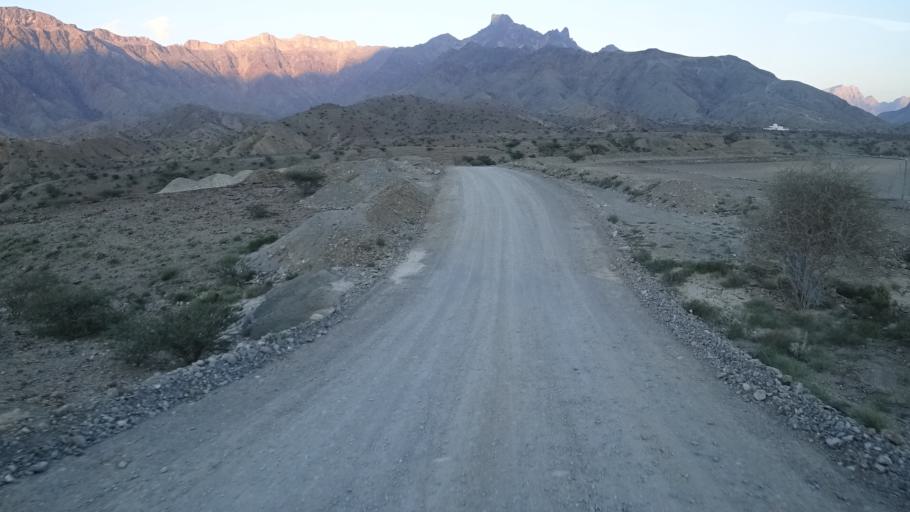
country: OM
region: Al Batinah
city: Rustaq
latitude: 23.2906
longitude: 57.3335
